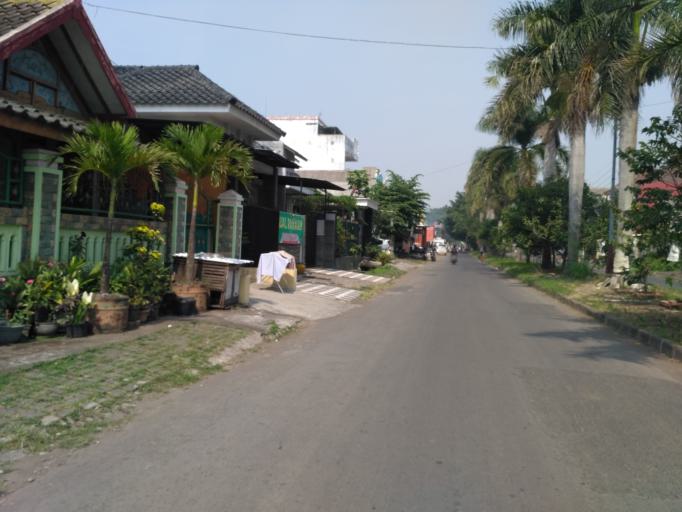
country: ID
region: East Java
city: Malang
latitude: -7.9667
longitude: 112.6657
